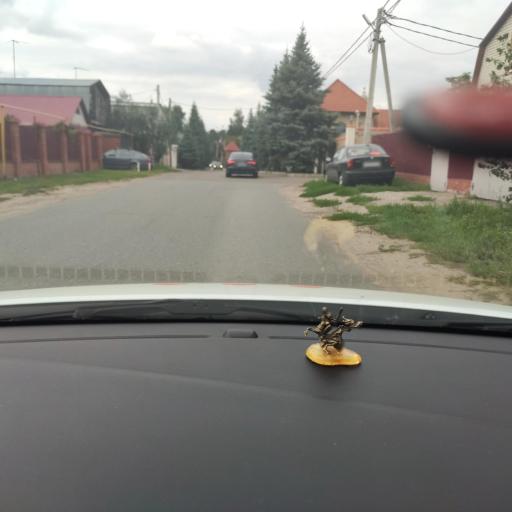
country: RU
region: Tatarstan
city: Verkhniy Uslon
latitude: 55.6171
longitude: 49.0160
